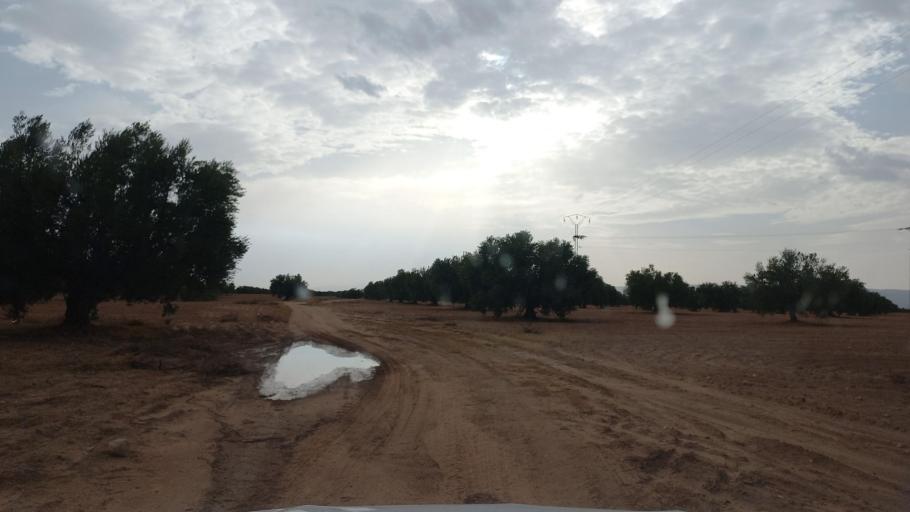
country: TN
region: Al Qasrayn
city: Sbiba
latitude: 35.2955
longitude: 9.0732
